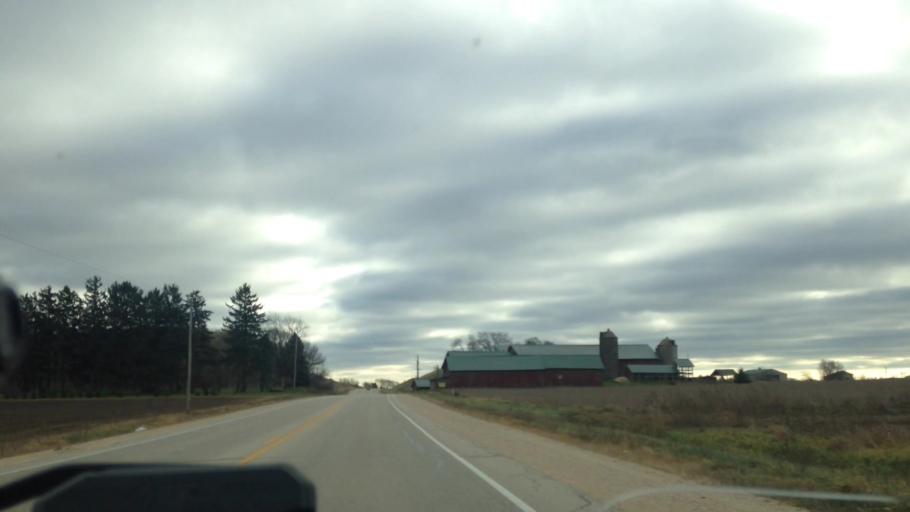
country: US
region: Wisconsin
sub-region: Dodge County
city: Theresa
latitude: 43.4350
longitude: -88.4642
